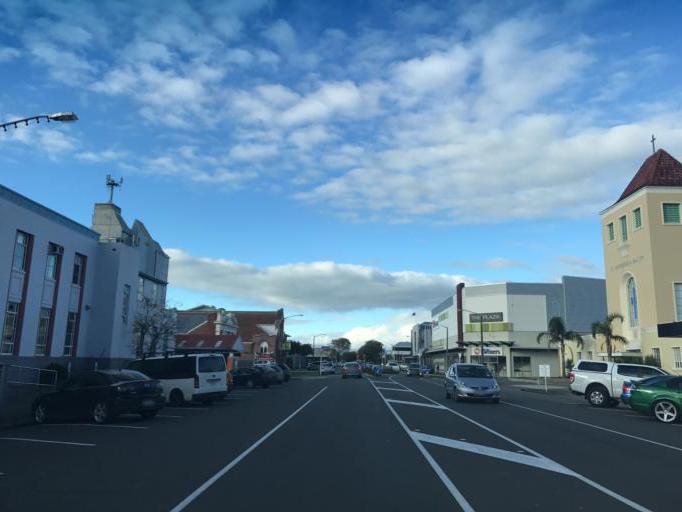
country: NZ
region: Manawatu-Wanganui
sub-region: Palmerston North City
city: Palmerston North
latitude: -40.3565
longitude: 175.6137
